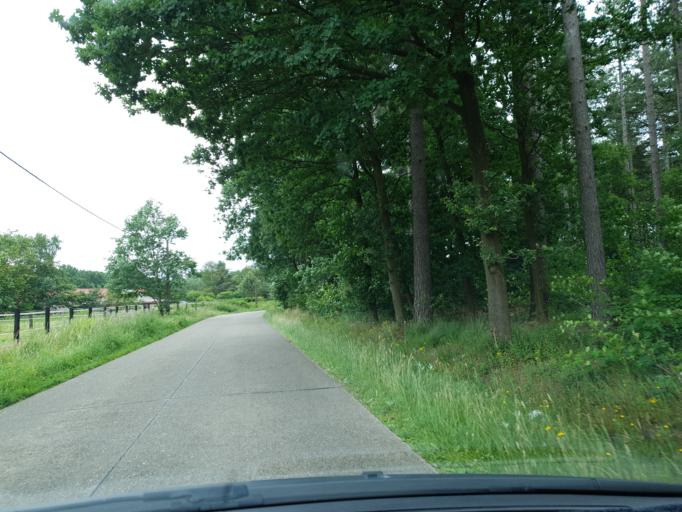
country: BE
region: Flanders
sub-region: Provincie Antwerpen
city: Westerlo
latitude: 51.0955
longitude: 4.8939
